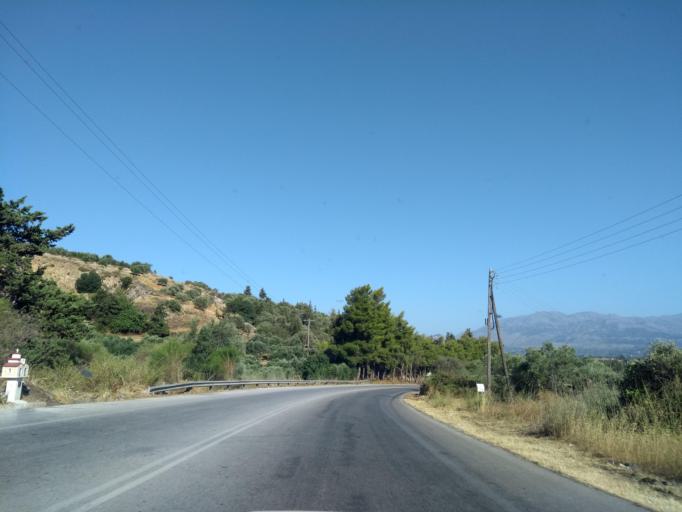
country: GR
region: Crete
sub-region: Nomos Chanias
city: Kalivai
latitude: 35.4068
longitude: 24.1480
